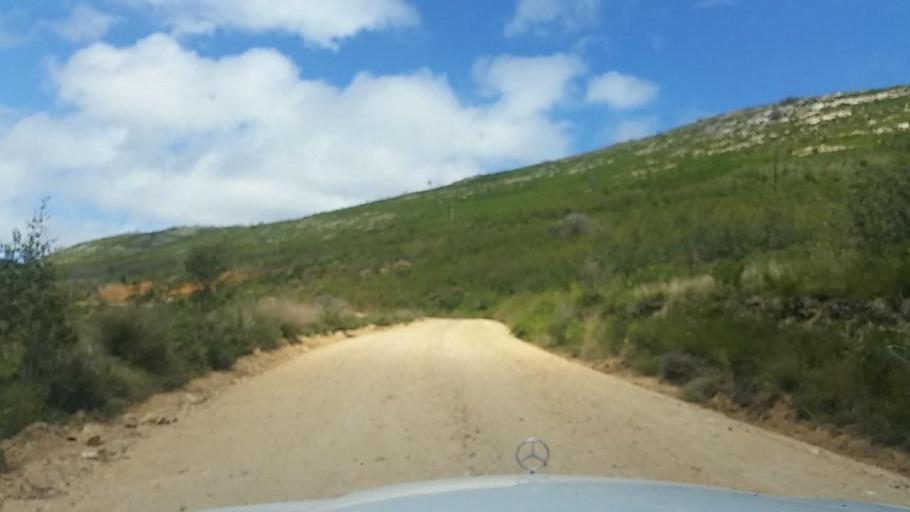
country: ZA
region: Western Cape
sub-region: Eden District Municipality
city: Knysna
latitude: -33.8862
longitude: 23.1603
